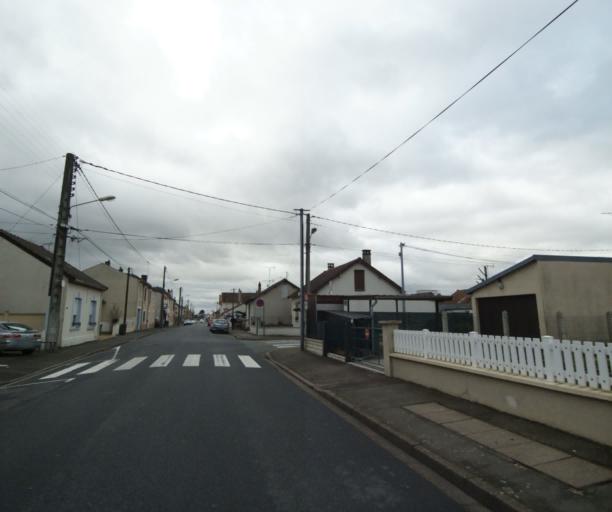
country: FR
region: Pays de la Loire
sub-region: Departement de la Sarthe
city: Le Mans
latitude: 47.9779
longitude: 0.2040
